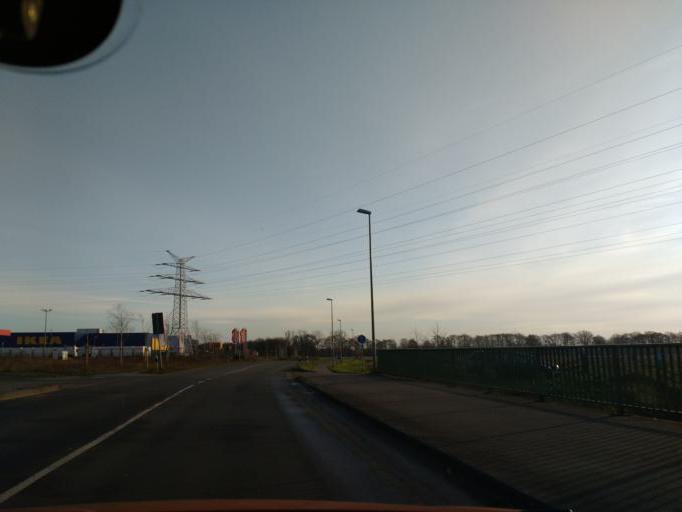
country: DE
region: Lower Saxony
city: Oldenburg
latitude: 53.1391
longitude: 8.2500
